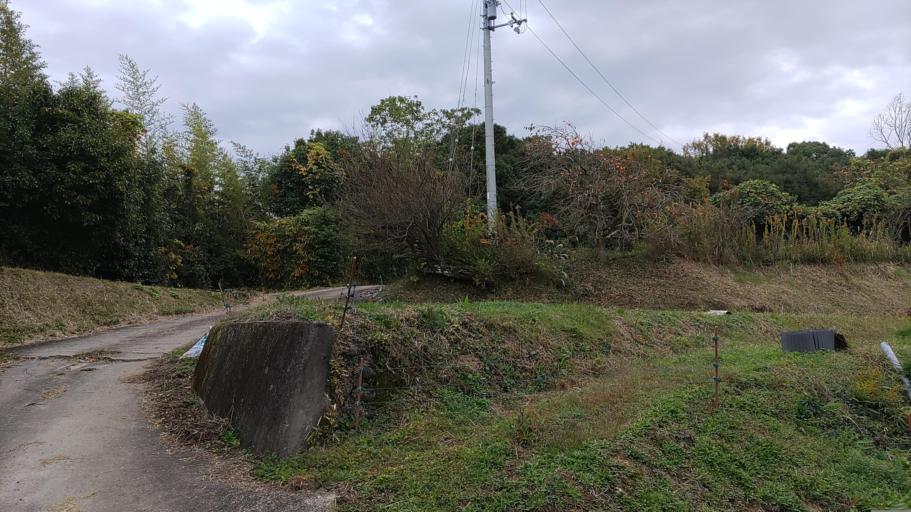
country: JP
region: Hyogo
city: Sumoto
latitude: 34.3850
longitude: 134.8143
